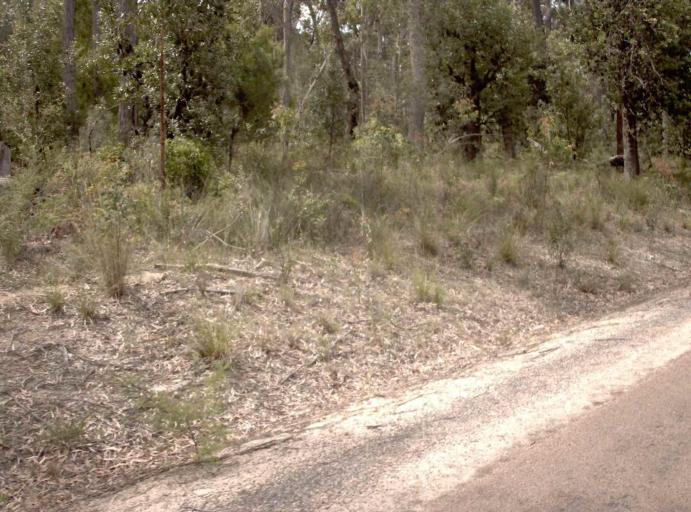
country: AU
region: New South Wales
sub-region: Bega Valley
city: Eden
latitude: -37.5039
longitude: 149.5343
